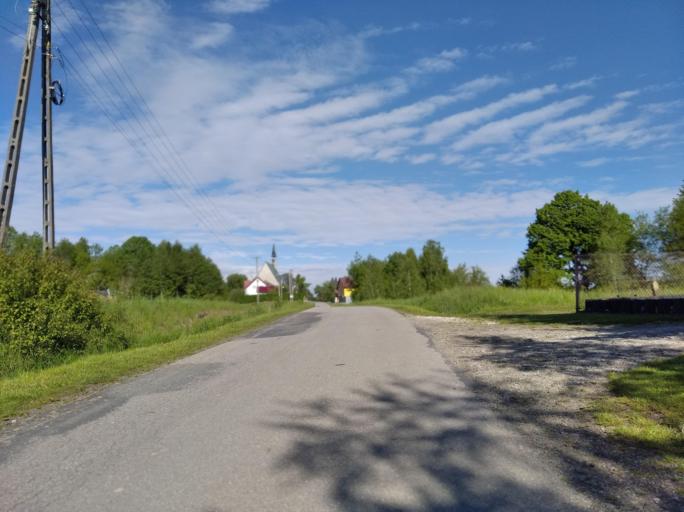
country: PL
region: Subcarpathian Voivodeship
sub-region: Powiat strzyzowski
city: Frysztak
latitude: 49.8470
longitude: 21.5332
